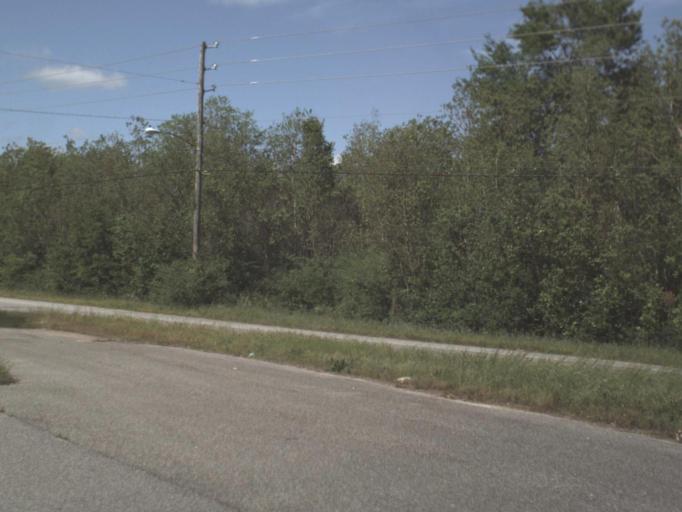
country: US
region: Florida
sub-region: Escambia County
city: Cantonment
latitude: 30.6049
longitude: -87.3161
